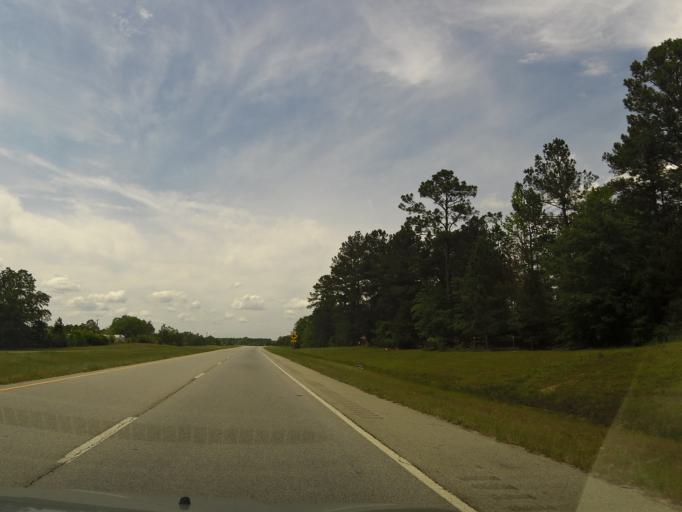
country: US
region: Georgia
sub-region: Emanuel County
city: Swainsboro
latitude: 32.5547
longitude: -82.3332
